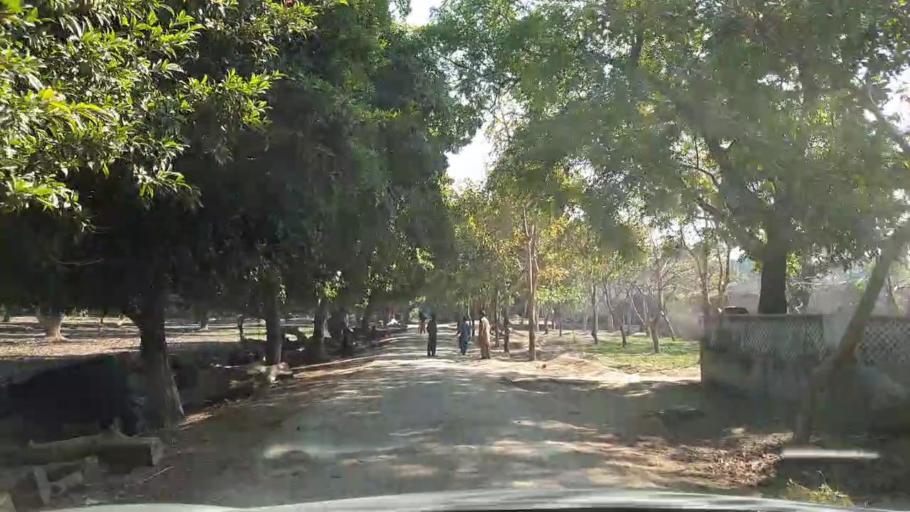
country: PK
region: Sindh
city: Tando Allahyar
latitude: 25.5224
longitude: 68.7108
